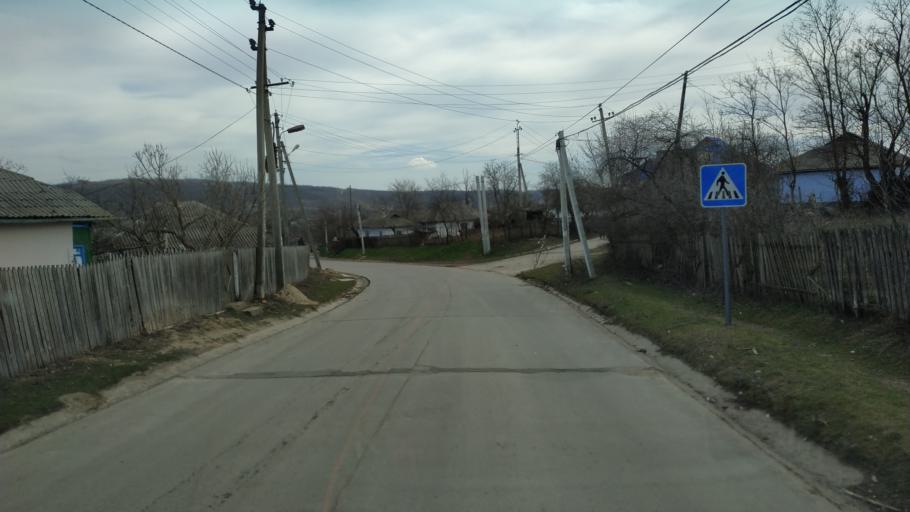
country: MD
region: Nisporeni
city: Nisporeni
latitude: 46.9266
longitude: 28.2620
